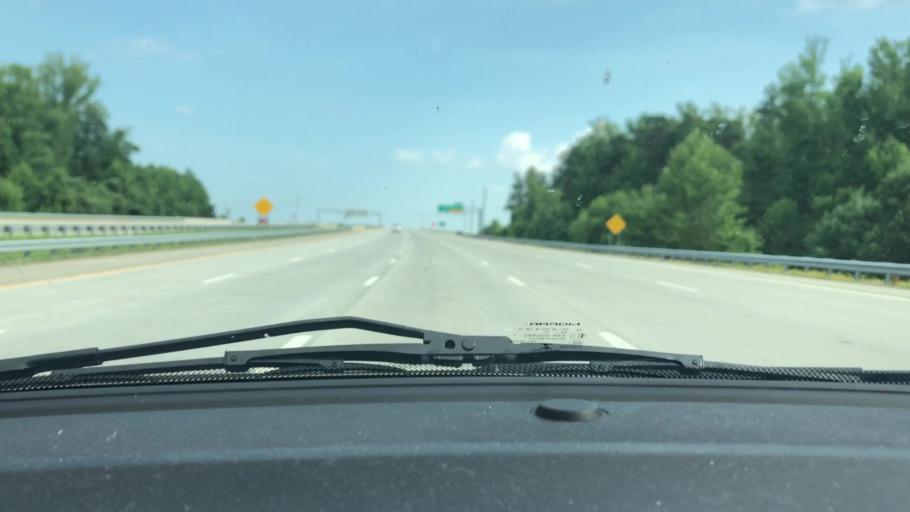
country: US
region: North Carolina
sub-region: Guilford County
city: Jamestown
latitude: 36.0556
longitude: -79.9191
